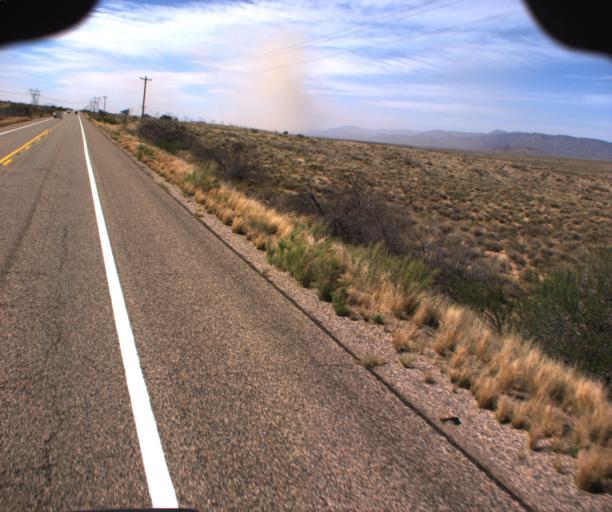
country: US
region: Arizona
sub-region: Mohave County
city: New Kingman-Butler
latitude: 35.3882
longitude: -113.7380
